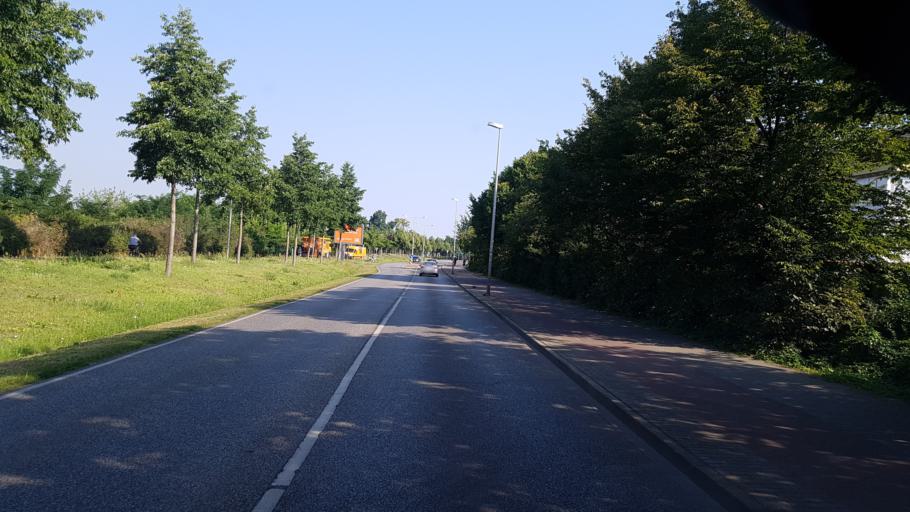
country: DE
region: Brandenburg
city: Cottbus
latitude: 51.7610
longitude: 14.3137
